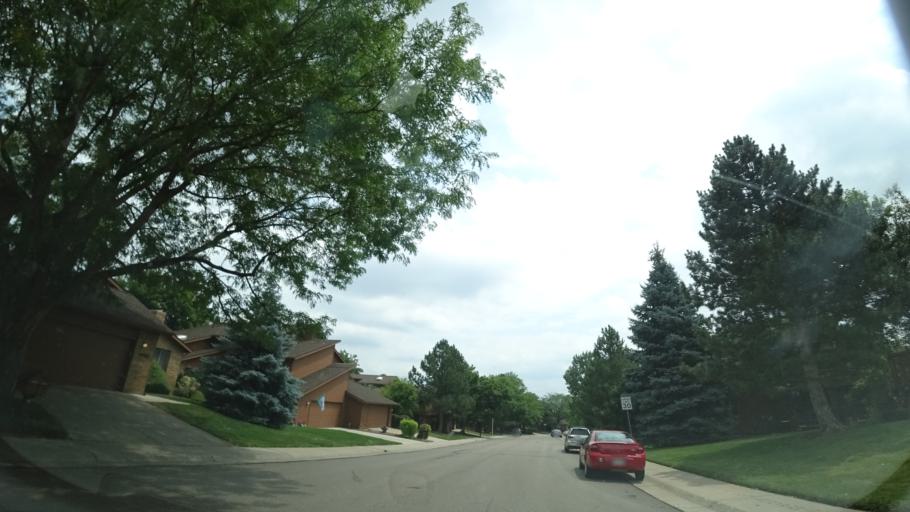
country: US
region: Colorado
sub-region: Jefferson County
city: West Pleasant View
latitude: 39.7197
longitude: -105.1447
